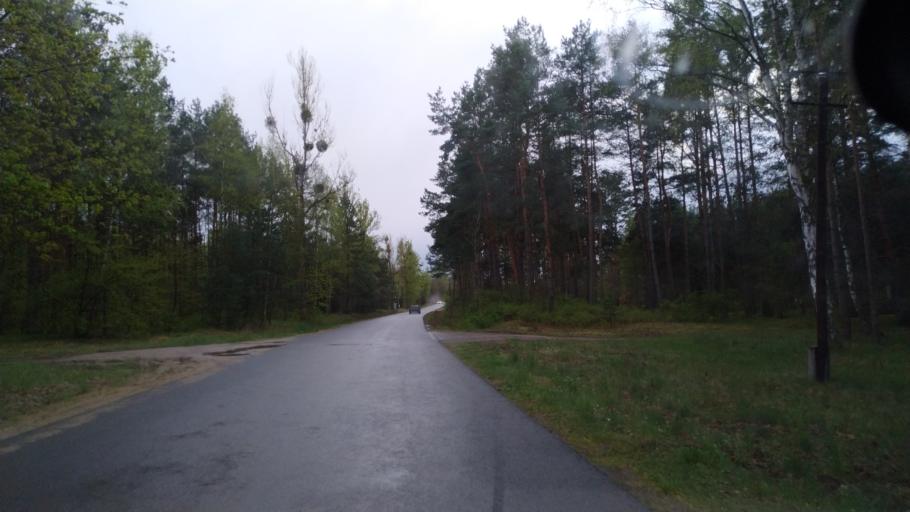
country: PL
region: Pomeranian Voivodeship
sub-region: Powiat starogardzki
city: Osiek
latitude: 53.6456
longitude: 18.4885
